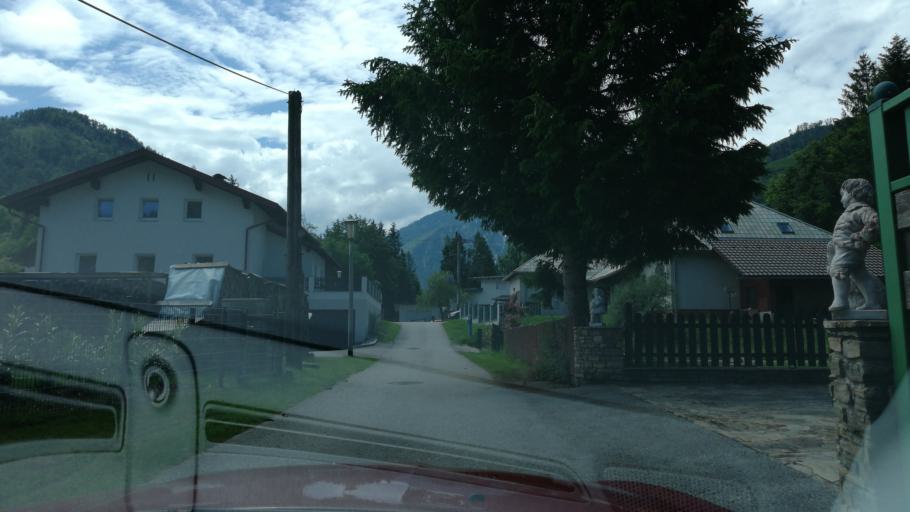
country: AT
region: Upper Austria
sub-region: Politischer Bezirk Kirchdorf an der Krems
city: Micheldorf in Oberoesterreich
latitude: 47.7770
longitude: 14.1733
